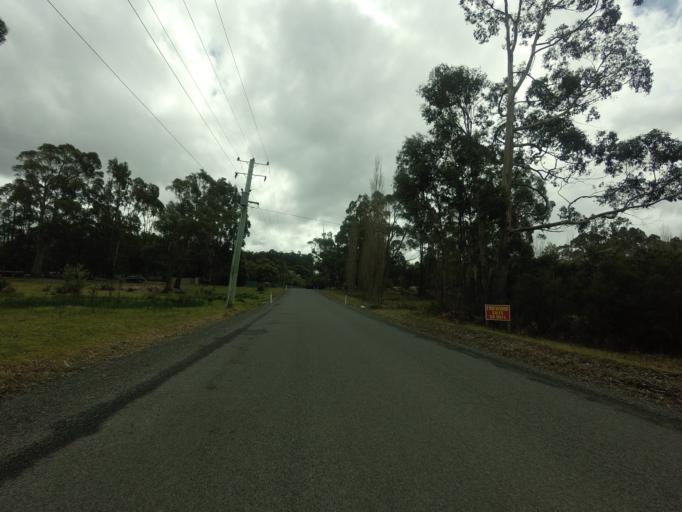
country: AU
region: Tasmania
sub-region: Huon Valley
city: Geeveston
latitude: -43.4317
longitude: 146.9035
